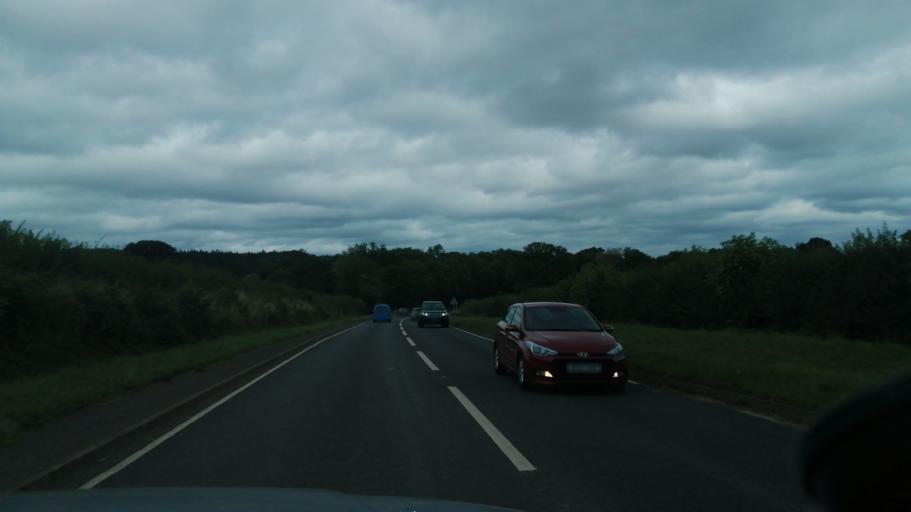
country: GB
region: England
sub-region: Herefordshire
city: Thruxton
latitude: 51.9773
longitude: -2.8283
